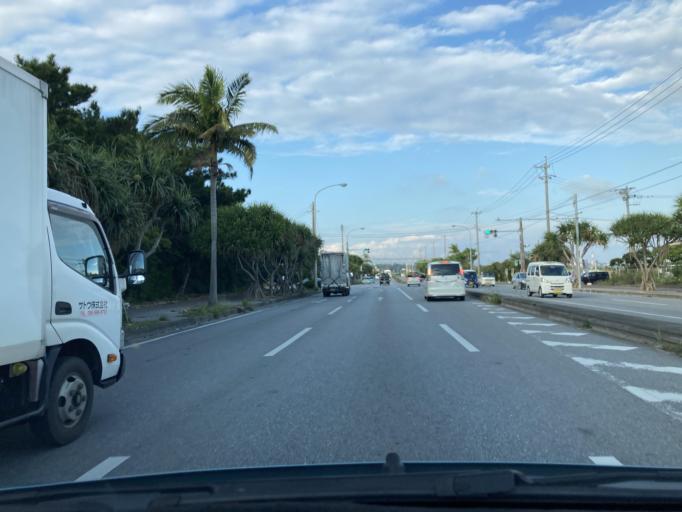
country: JP
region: Okinawa
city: Okinawa
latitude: 26.3237
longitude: 127.8335
